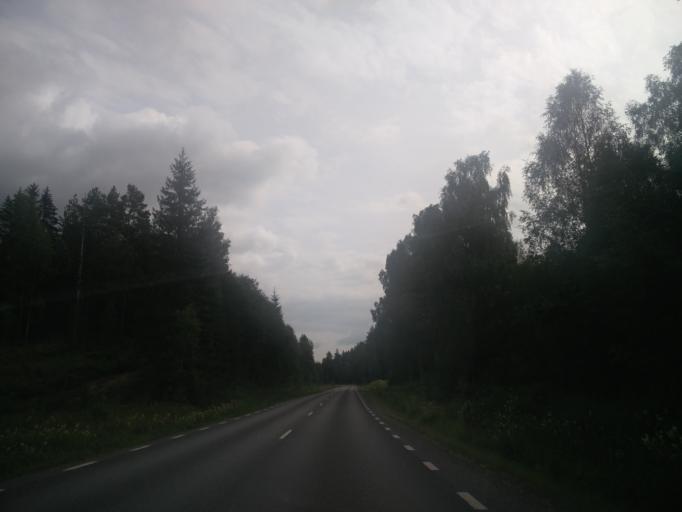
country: SE
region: Vaermland
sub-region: Arvika Kommun
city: Arvika
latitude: 59.7210
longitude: 12.5681
